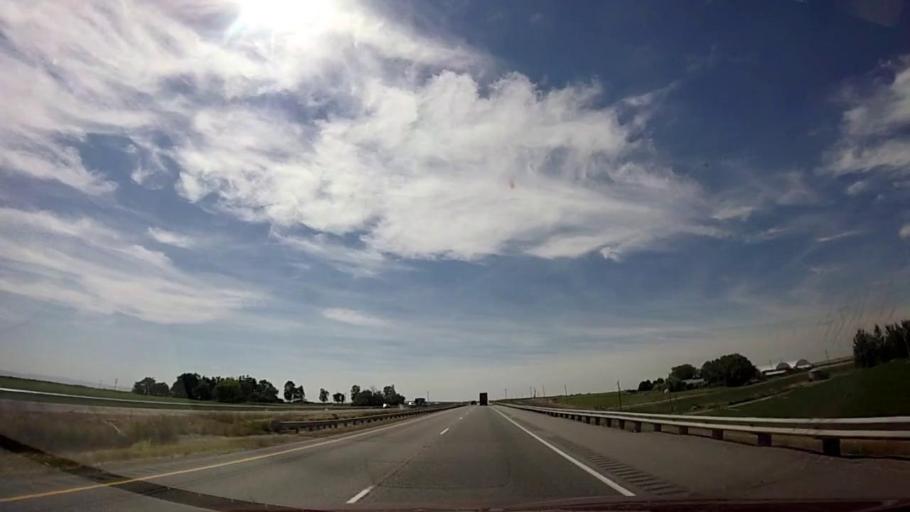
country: US
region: Idaho
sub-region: Cassia County
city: Burley
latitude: 42.5764
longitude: -113.9882
